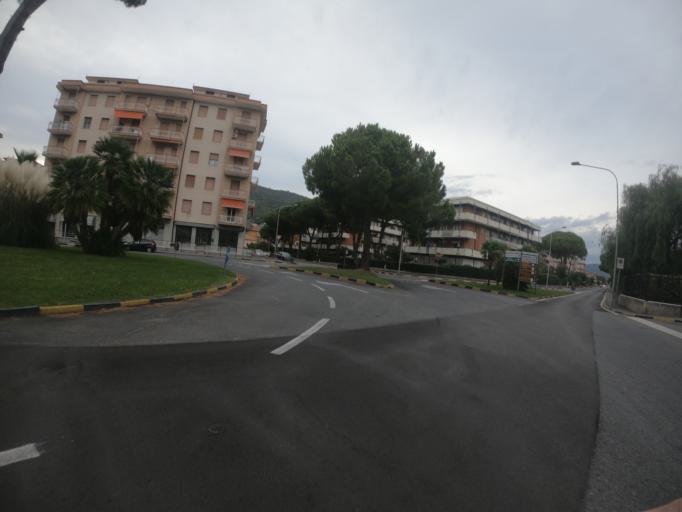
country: IT
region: Liguria
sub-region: Provincia di Savona
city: Marina di Andora
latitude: 43.9542
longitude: 8.1482
